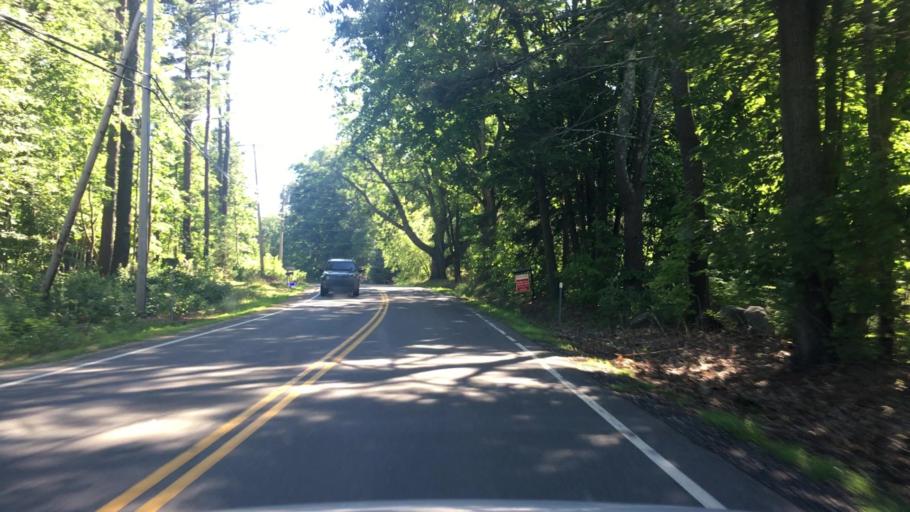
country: US
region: New Hampshire
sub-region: Rockingham County
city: Newmarket
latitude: 43.0366
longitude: -70.9526
